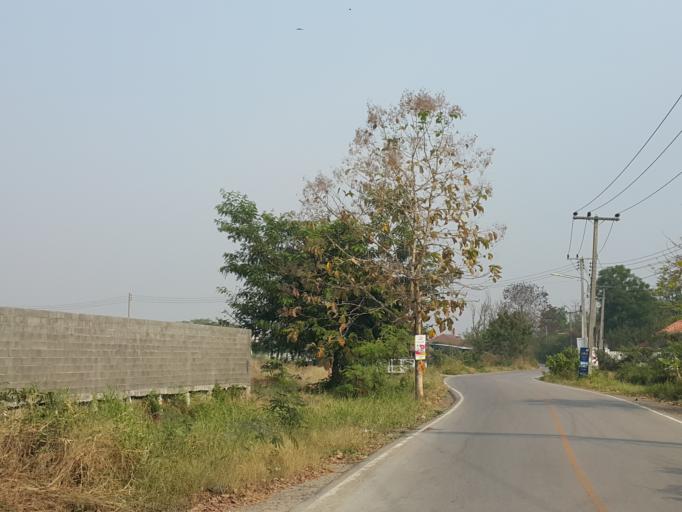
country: TH
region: Chiang Mai
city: San Kamphaeng
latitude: 18.7458
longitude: 99.0778
